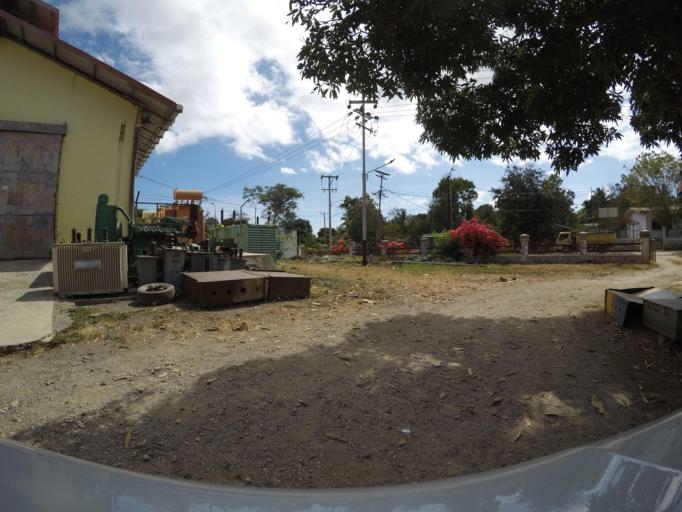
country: TL
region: Baucau
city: Baucau
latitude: -8.4833
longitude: 126.4567
